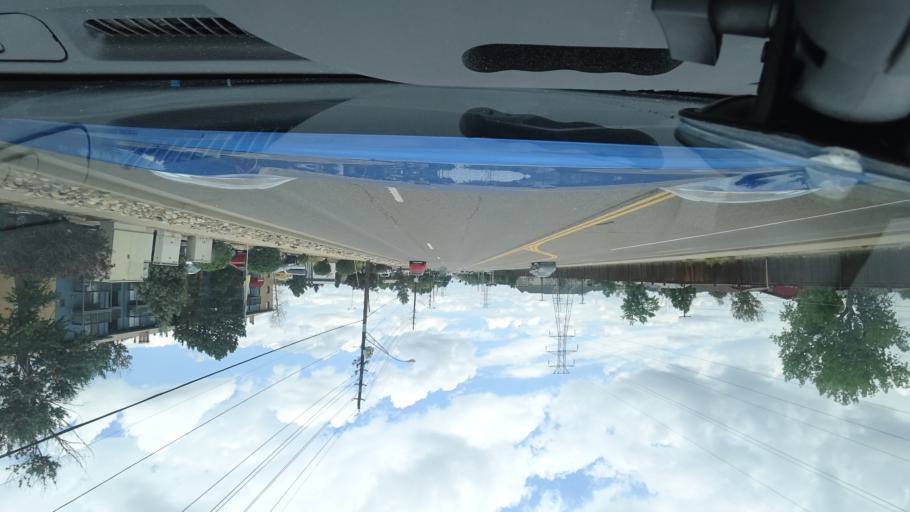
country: US
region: Colorado
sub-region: Adams County
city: Aurora
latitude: 39.7238
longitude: -104.8283
